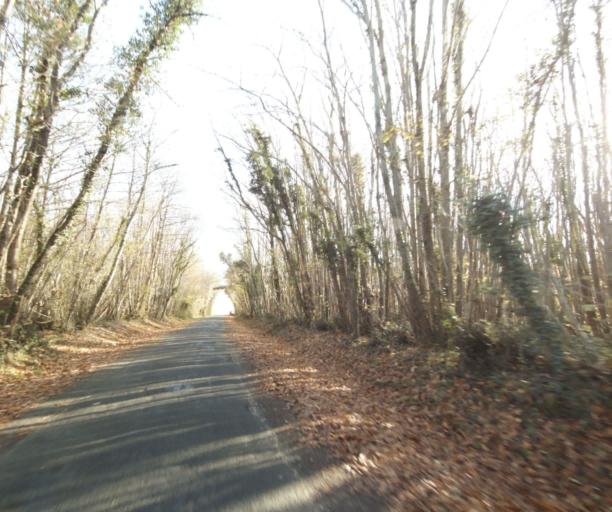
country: FR
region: Poitou-Charentes
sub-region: Departement de la Charente-Maritime
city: Cherac
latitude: 45.7418
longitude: -0.4617
